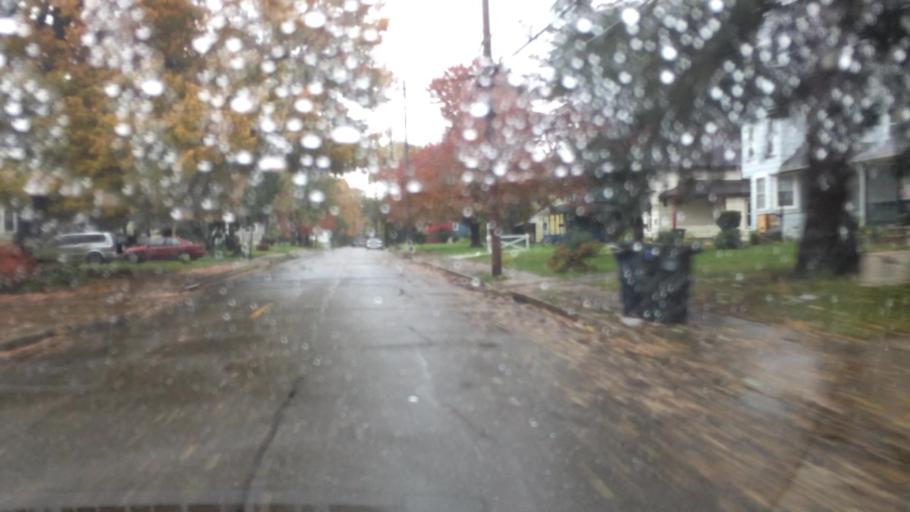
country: US
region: Ohio
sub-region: Summit County
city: Akron
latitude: 41.1019
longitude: -81.5078
